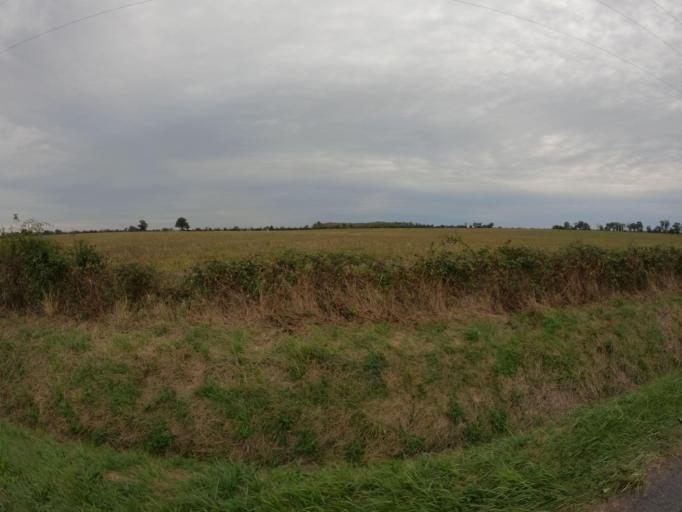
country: FR
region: Poitou-Charentes
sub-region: Departement de la Vienne
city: Saulge
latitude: 46.3707
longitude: 0.8416
